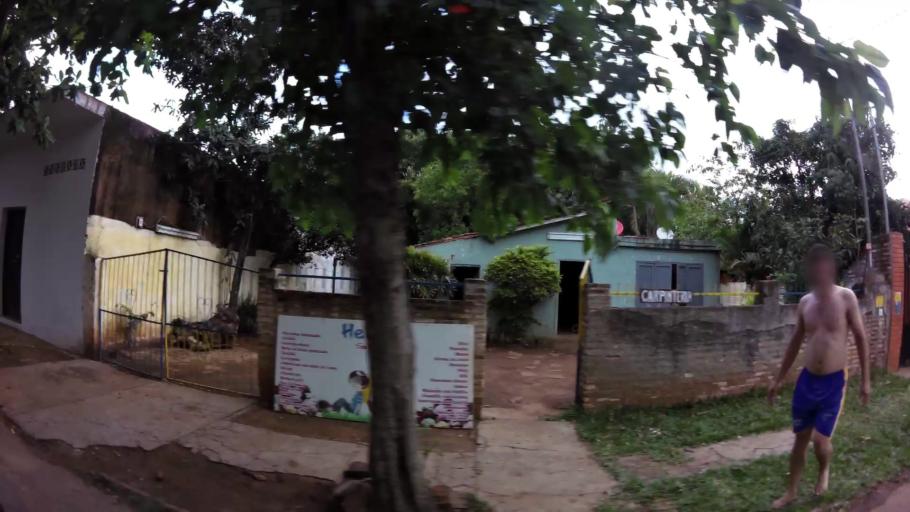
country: PY
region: Central
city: San Lorenzo
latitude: -25.2753
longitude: -57.4887
